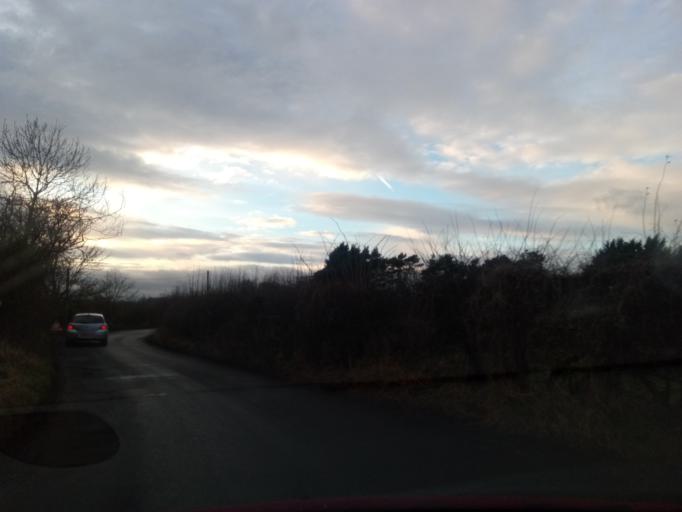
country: GB
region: England
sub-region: Northumberland
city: Ponteland
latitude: 55.0846
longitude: -1.7433
